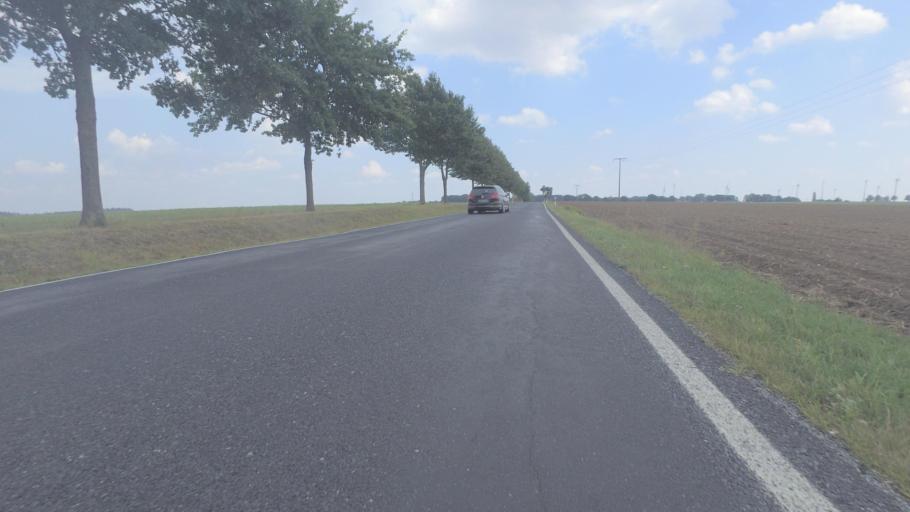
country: DE
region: Mecklenburg-Vorpommern
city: Borrentin
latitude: 53.8505
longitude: 12.9842
